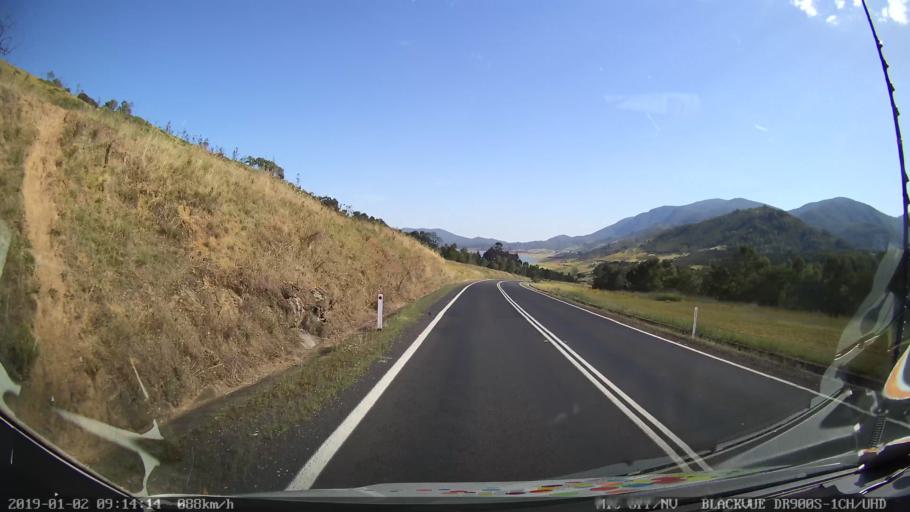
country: AU
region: New South Wales
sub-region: Tumut Shire
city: Tumut
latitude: -35.4799
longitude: 148.2728
